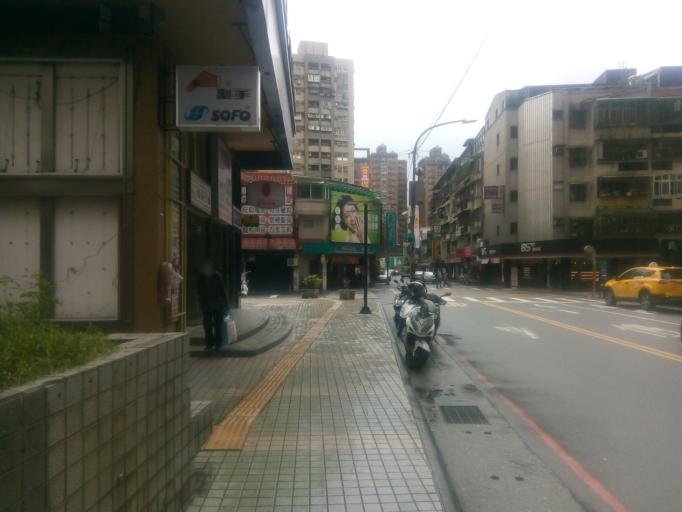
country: TW
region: Taiwan
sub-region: Keelung
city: Keelung
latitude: 25.0729
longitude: 121.6632
